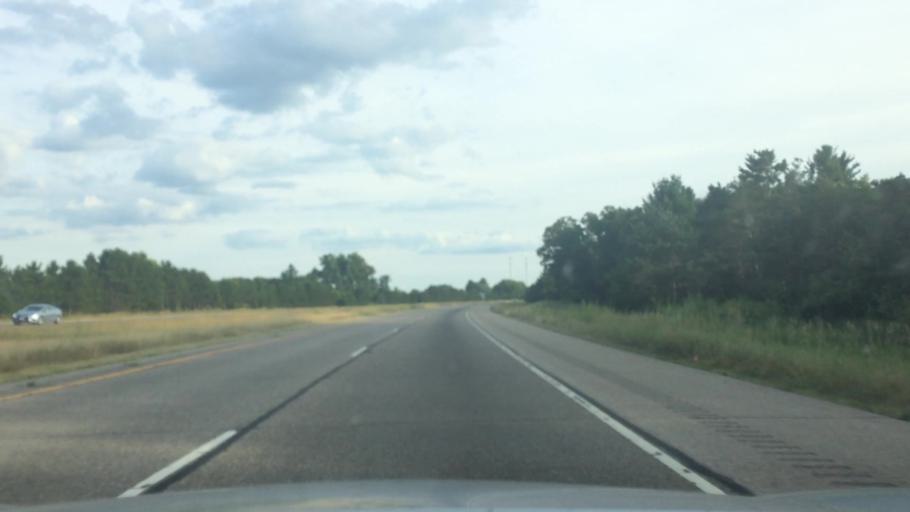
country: US
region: Wisconsin
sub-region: Portage County
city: Plover
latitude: 44.2002
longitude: -89.5231
